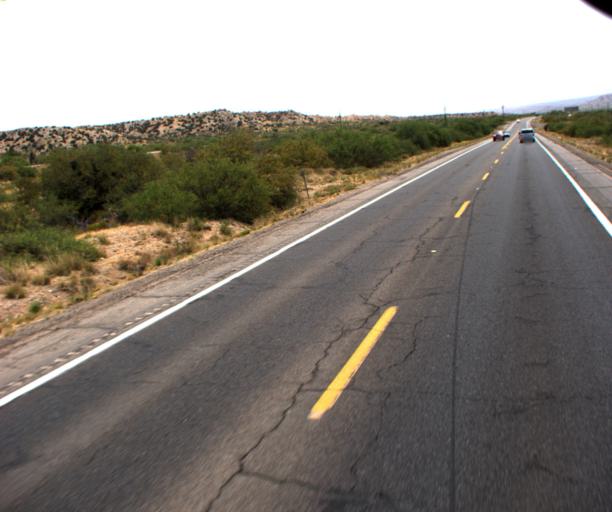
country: US
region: Arizona
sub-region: Gila County
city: Globe
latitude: 33.3684
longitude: -110.7226
